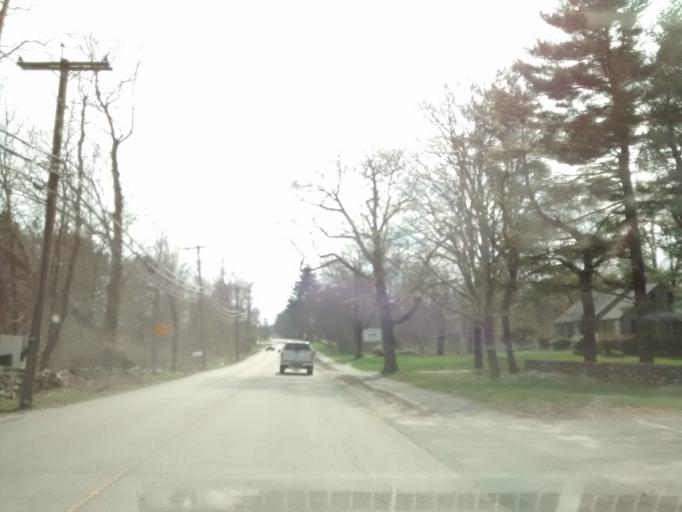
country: US
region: Massachusetts
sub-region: Worcester County
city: Sutton
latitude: 42.1470
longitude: -71.7686
